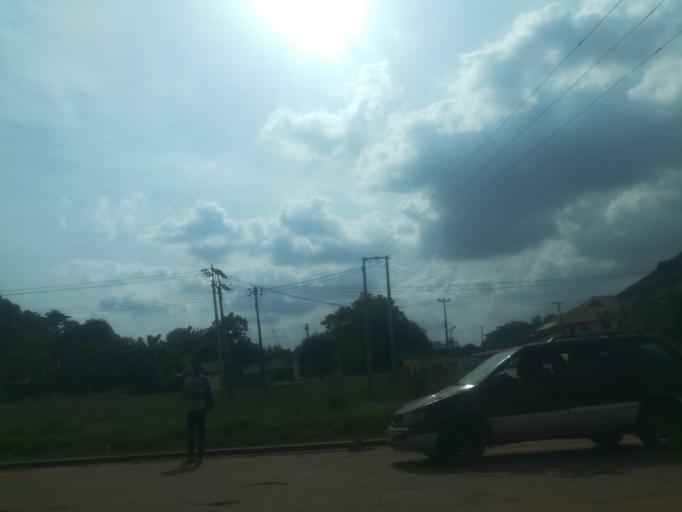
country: NG
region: Ogun
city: Abeokuta
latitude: 7.1316
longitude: 3.3538
